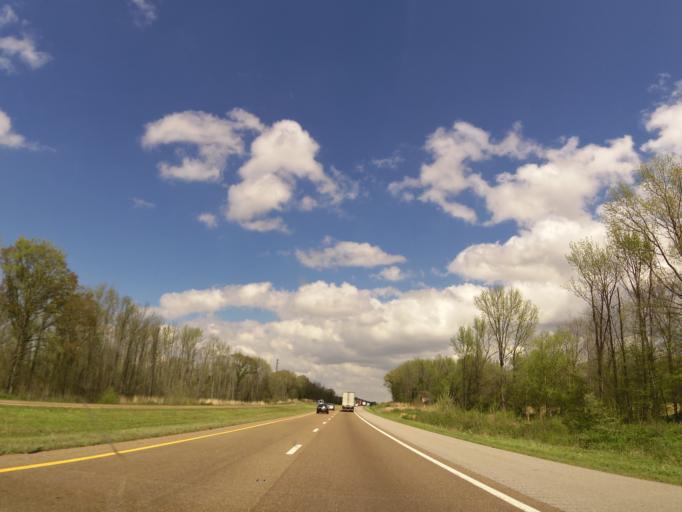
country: US
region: Tennessee
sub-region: Tipton County
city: Mason
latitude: 35.3297
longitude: -89.5576
